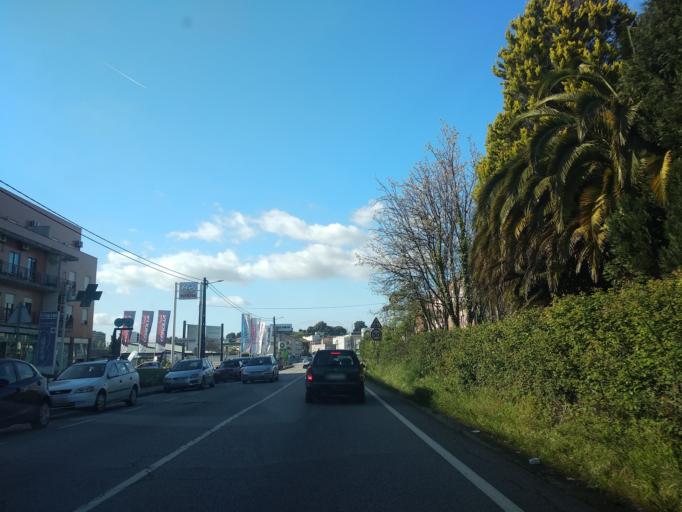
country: PT
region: Braga
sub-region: Braga
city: Braga
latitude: 41.5299
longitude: -8.4184
